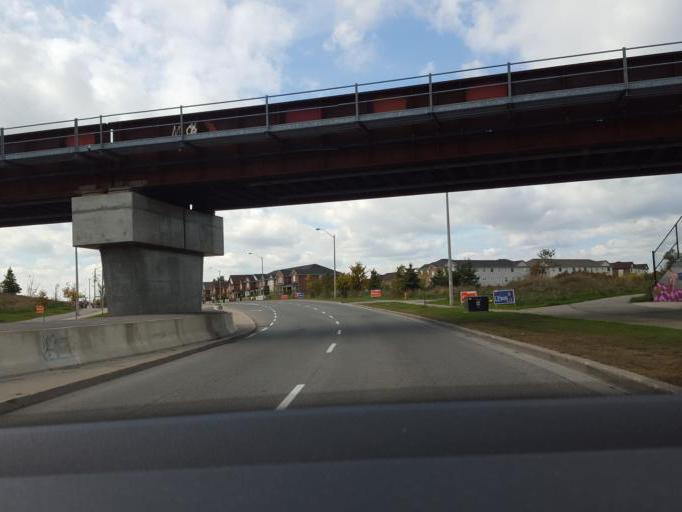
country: CA
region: Ontario
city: Scarborough
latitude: 43.8200
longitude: -79.2172
